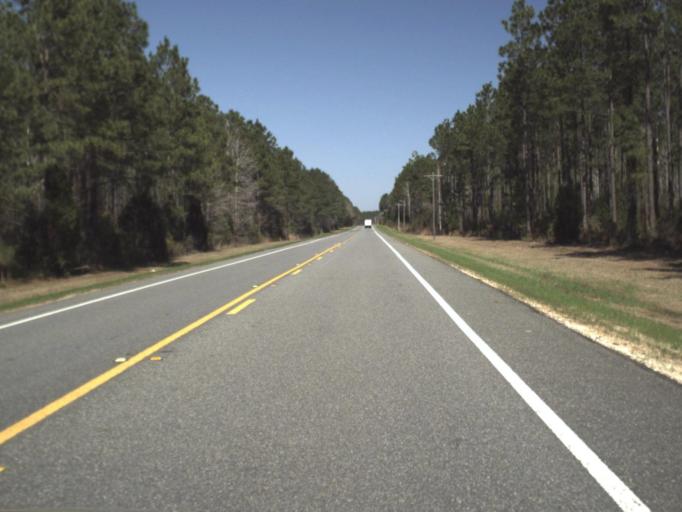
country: US
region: Florida
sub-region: Calhoun County
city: Blountstown
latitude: 30.3325
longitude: -85.1250
